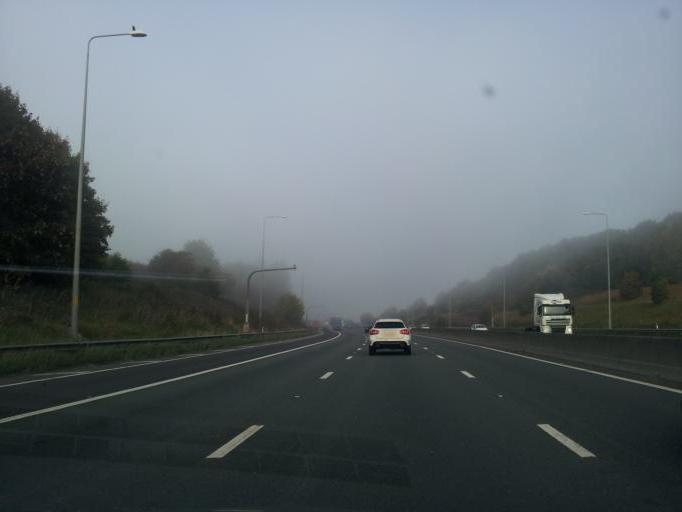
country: GB
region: England
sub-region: Kirklees
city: Cleckheaton
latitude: 53.7445
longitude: -1.7002
